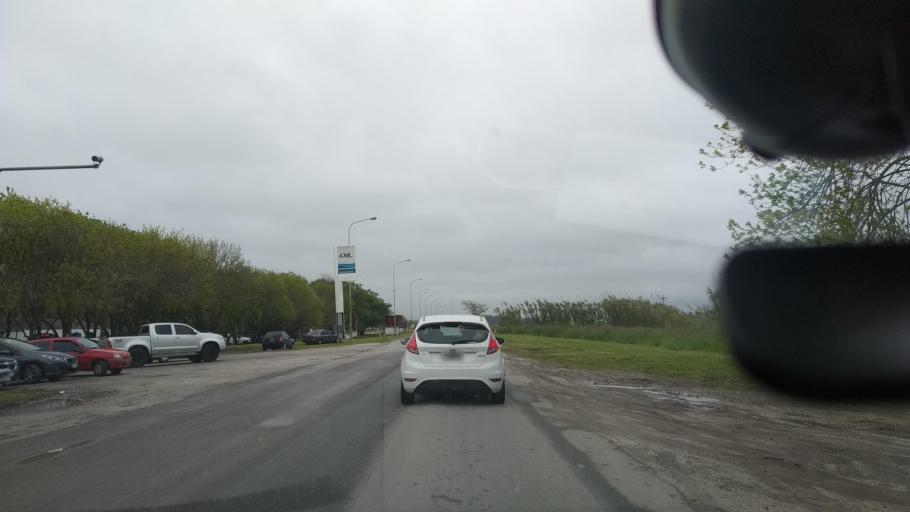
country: AR
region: Buenos Aires
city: Veronica
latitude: -35.5306
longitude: -57.3231
